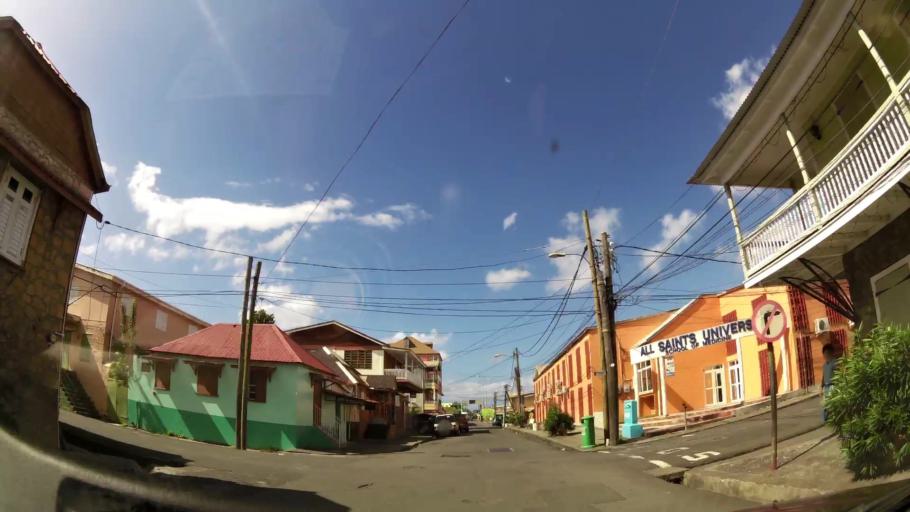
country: DM
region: Saint George
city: Roseau
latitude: 15.2996
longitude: -61.3880
